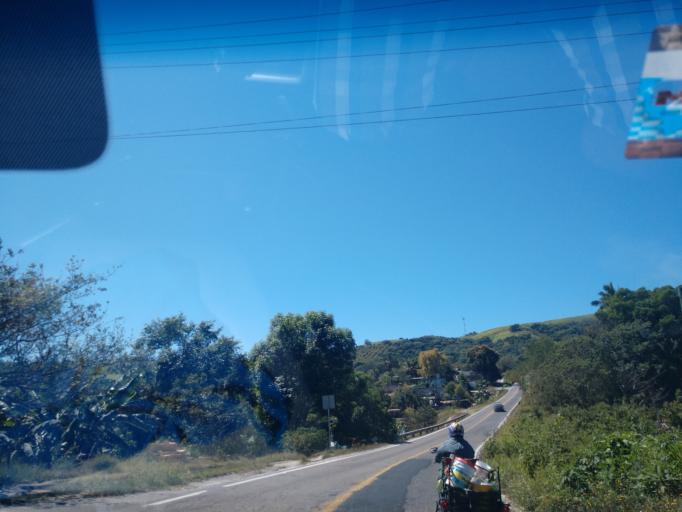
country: MX
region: Nayarit
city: Xalisco
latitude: 21.3664
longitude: -104.9156
